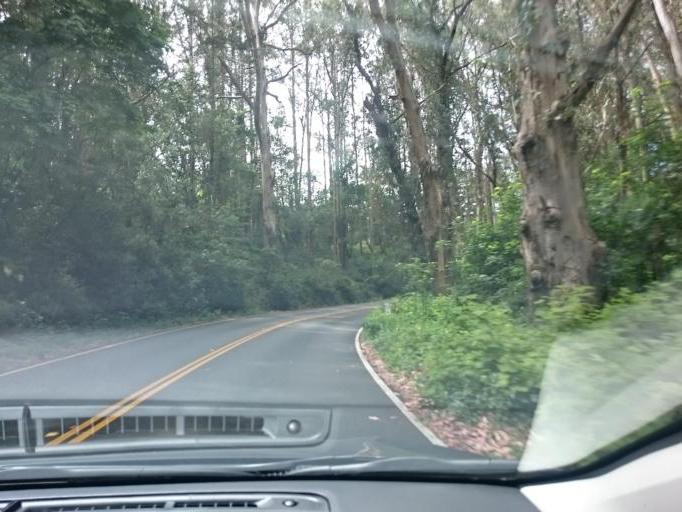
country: US
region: California
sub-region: Marin County
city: Bolinas
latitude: 37.9593
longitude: -122.7195
